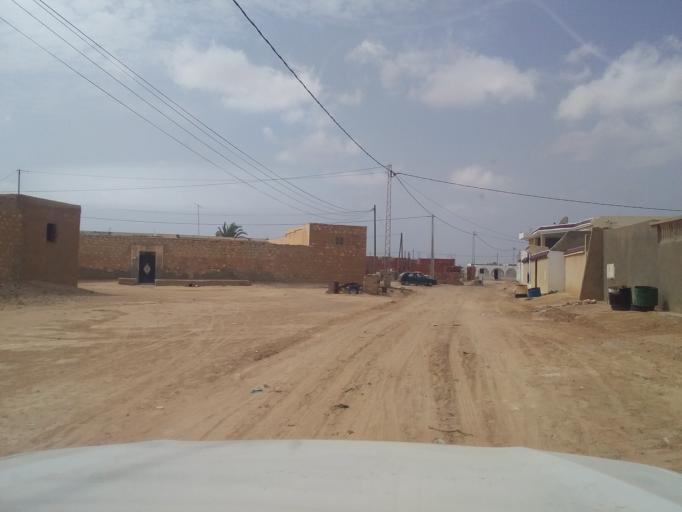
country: TN
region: Qabis
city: Matmata
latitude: 33.6199
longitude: 10.2631
